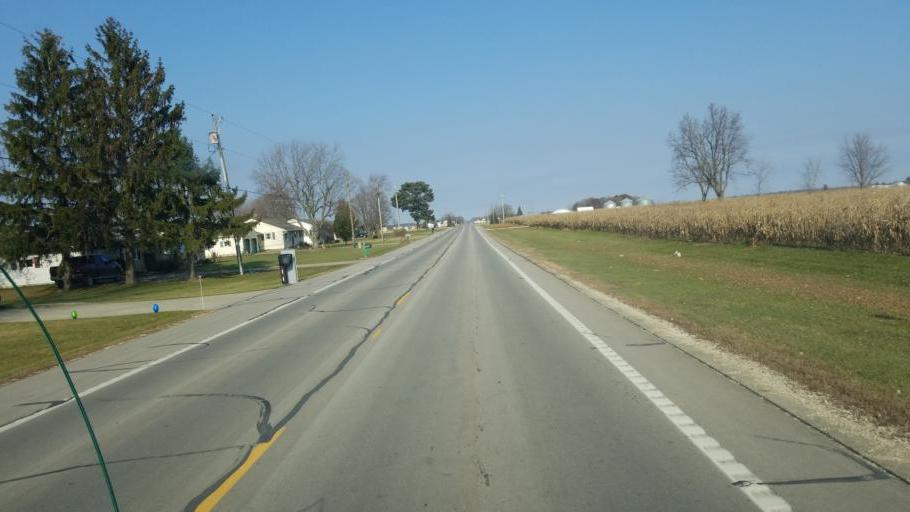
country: US
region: Ohio
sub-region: Mercer County
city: Coldwater
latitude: 40.5103
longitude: -84.6286
